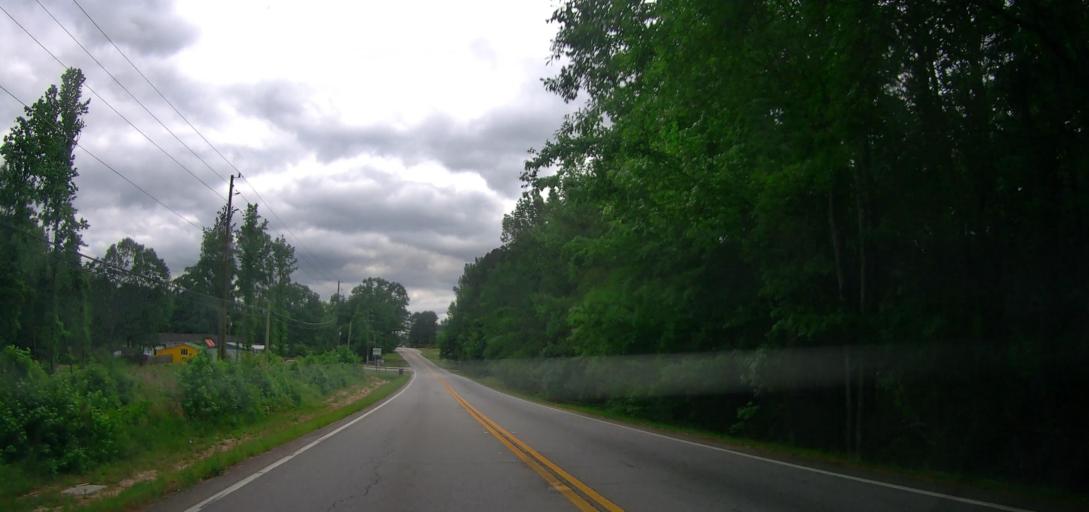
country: US
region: Georgia
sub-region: Henry County
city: Stockbridge
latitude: 33.5655
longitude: -84.1672
